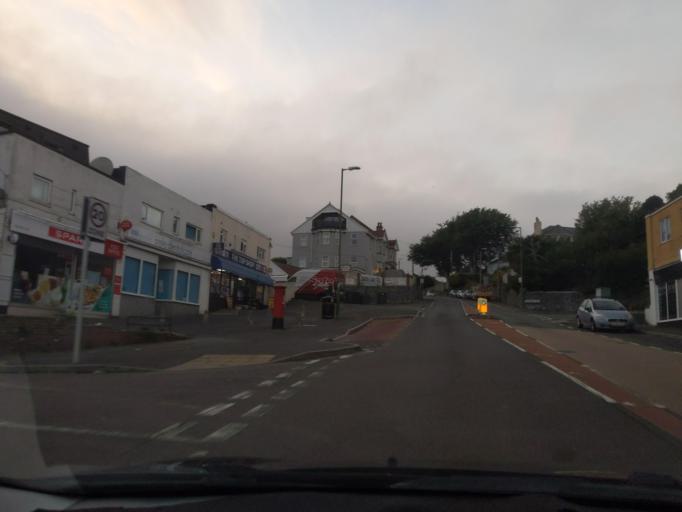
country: GB
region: England
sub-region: Devon
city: Marldon
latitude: 50.4452
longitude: -3.5834
